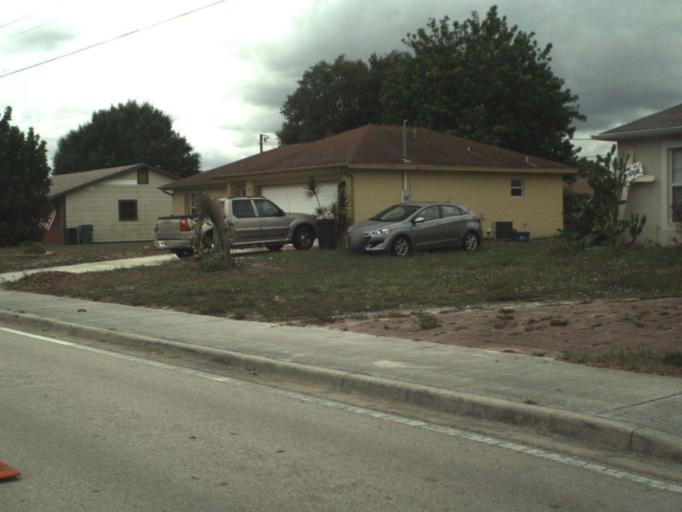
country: US
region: Florida
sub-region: Saint Lucie County
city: Port Saint Lucie
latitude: 27.3041
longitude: -80.3497
